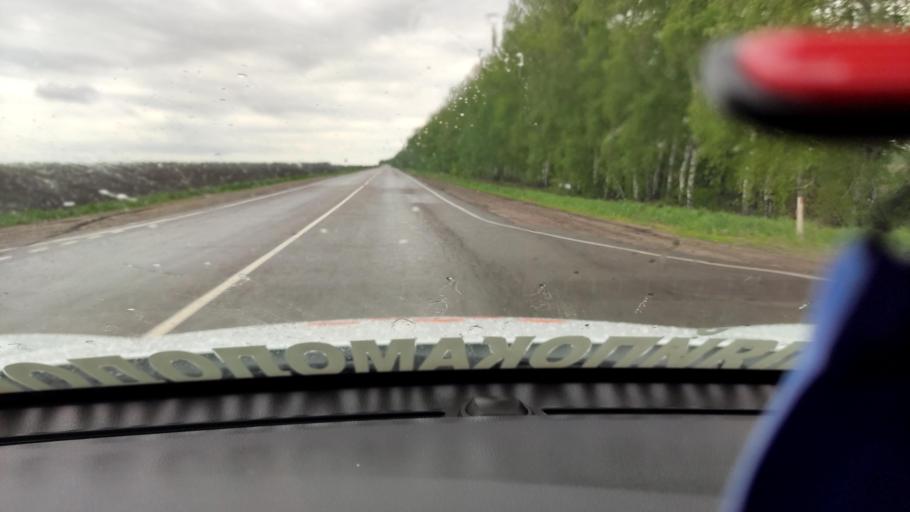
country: RU
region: Voronezj
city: Sredniy Ikorets
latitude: 51.0387
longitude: 39.6544
